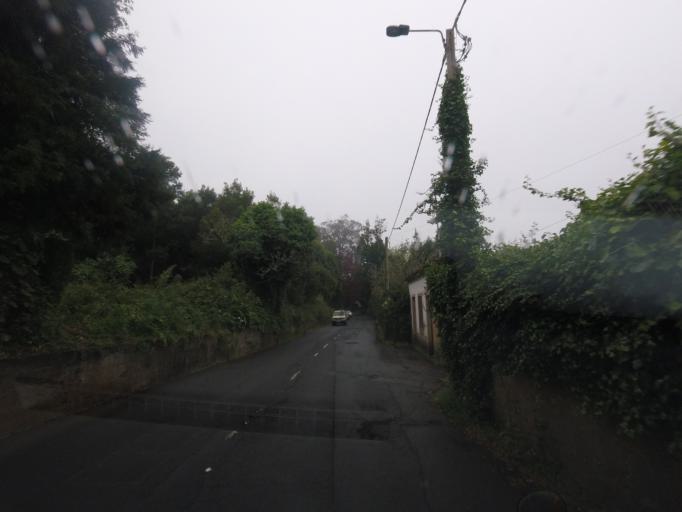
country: PT
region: Madeira
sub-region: Santa Cruz
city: Santa Cruz
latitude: 32.7234
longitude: -16.8171
